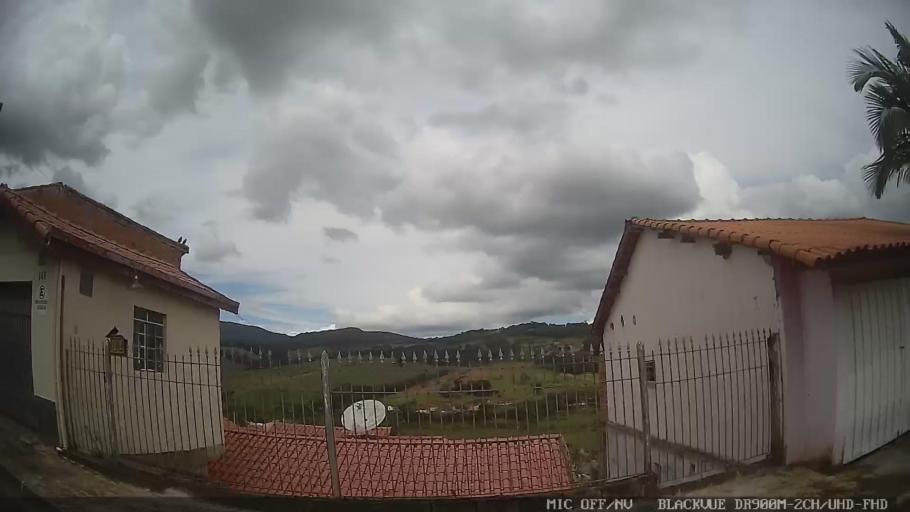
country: BR
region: Minas Gerais
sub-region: Extrema
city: Extrema
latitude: -22.7423
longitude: -46.3709
